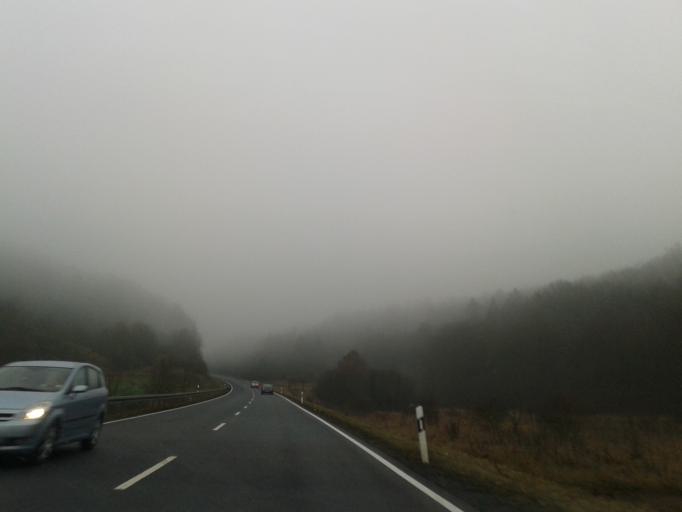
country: DE
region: Bavaria
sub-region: Regierungsbezirk Unterfranken
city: Hofheim in Unterfranken
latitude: 50.1271
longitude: 10.5747
